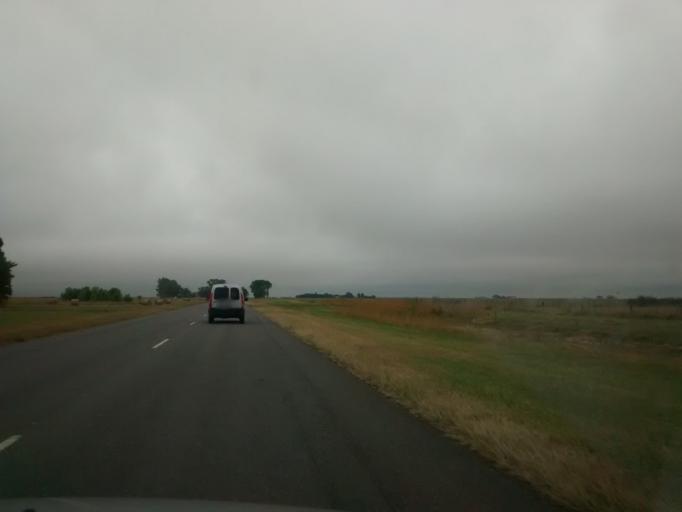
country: AR
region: Buenos Aires
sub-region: Partido de Ayacucho
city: Ayacucho
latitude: -37.2435
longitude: -58.4892
